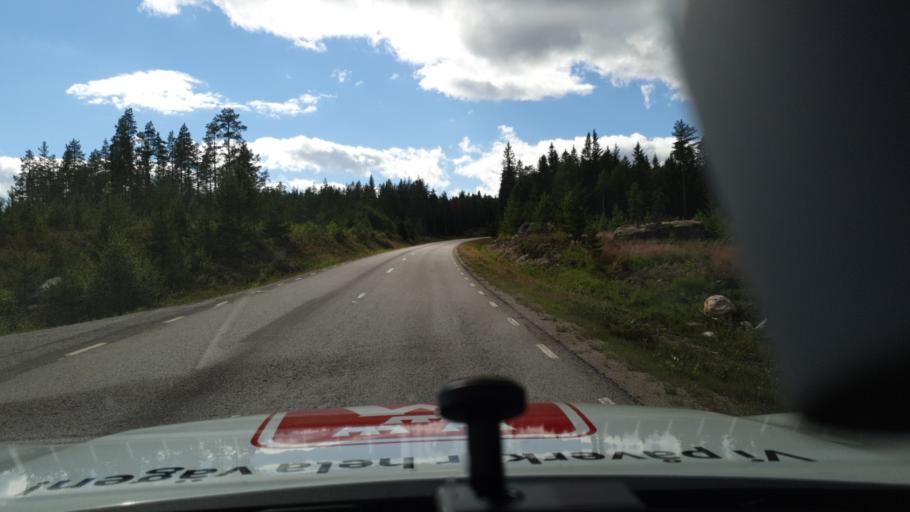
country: NO
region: Hedmark
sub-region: Trysil
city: Innbygda
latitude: 61.0184
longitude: 12.5331
